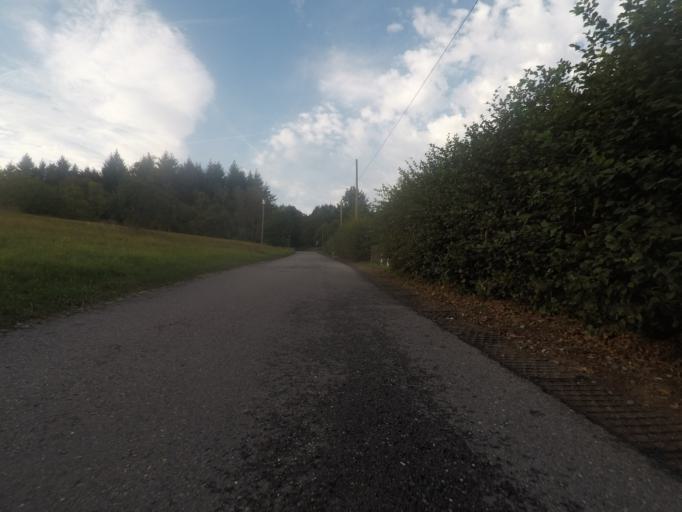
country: DE
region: Baden-Wuerttemberg
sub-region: Karlsruhe Region
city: Ettlingen
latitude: 48.8971
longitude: 8.4051
